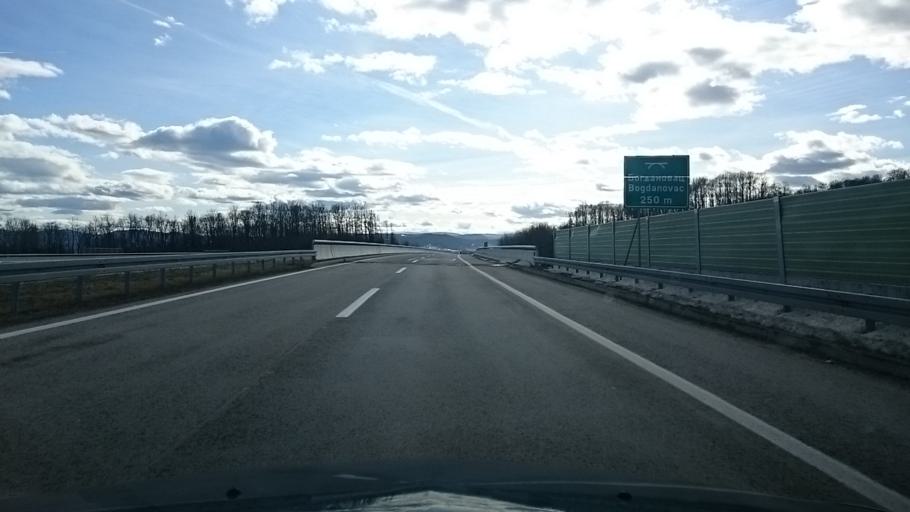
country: BA
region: Republika Srpska
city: Laktasi
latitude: 44.9058
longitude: 17.2948
